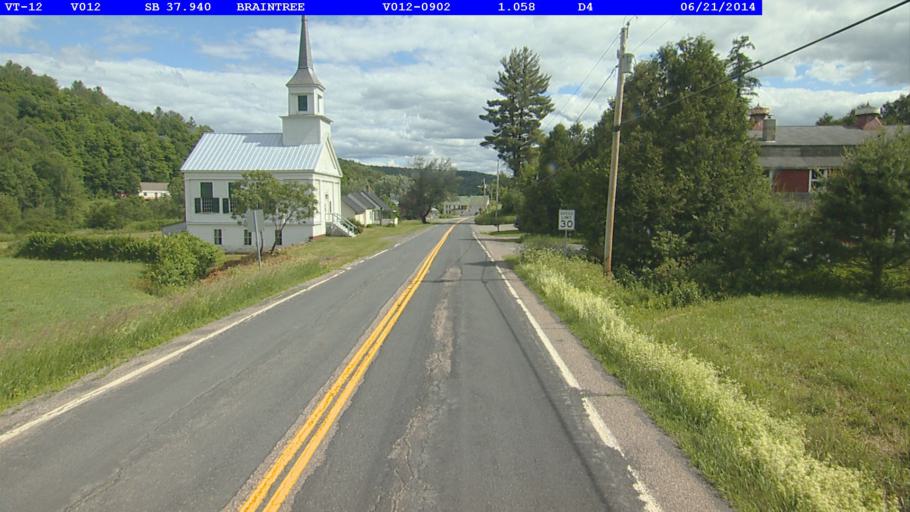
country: US
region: Vermont
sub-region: Orange County
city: Randolph
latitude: 43.9983
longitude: -72.6531
